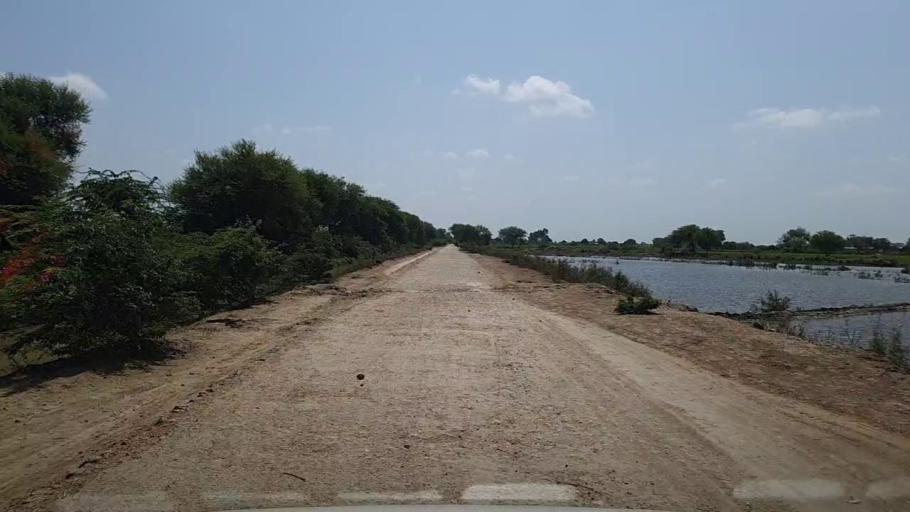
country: PK
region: Sindh
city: Kario
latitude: 24.8724
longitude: 68.6878
